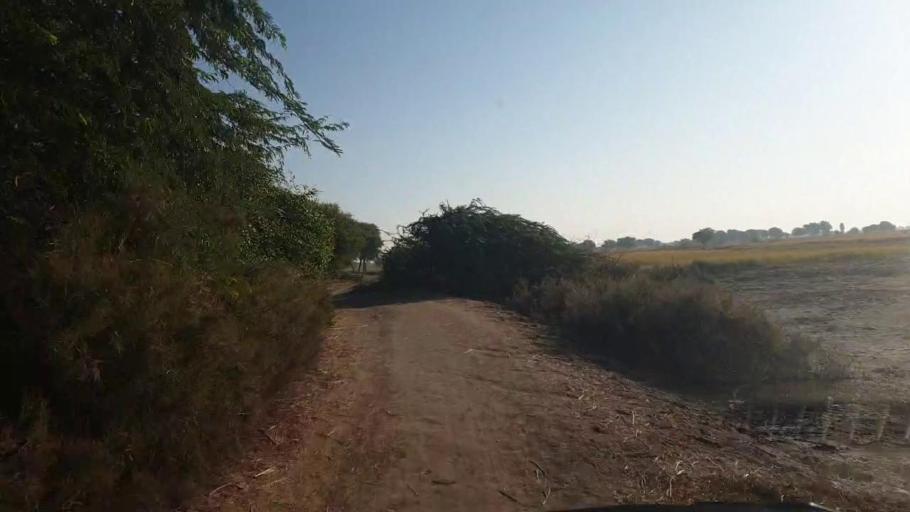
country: PK
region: Sindh
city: Talhar
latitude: 24.8044
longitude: 68.8254
